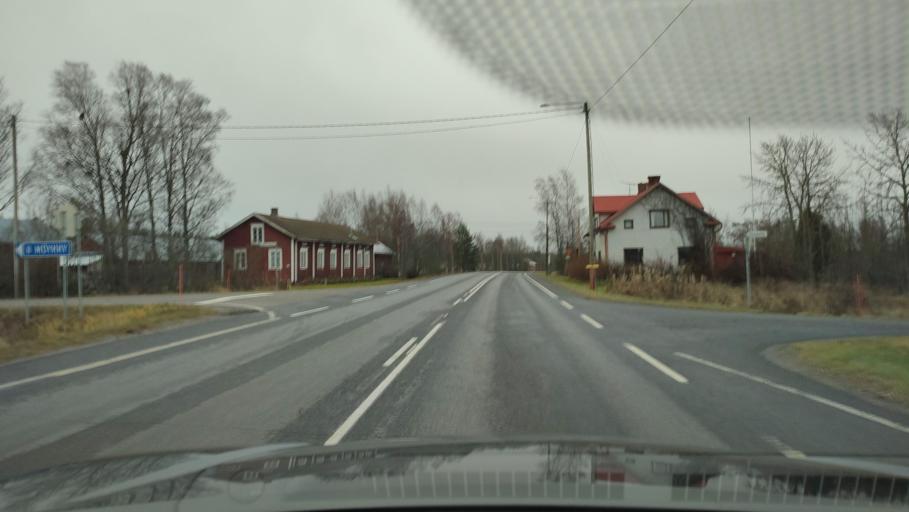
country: FI
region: Southern Ostrobothnia
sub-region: Suupohja
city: Isojoki
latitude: 62.1576
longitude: 21.8797
